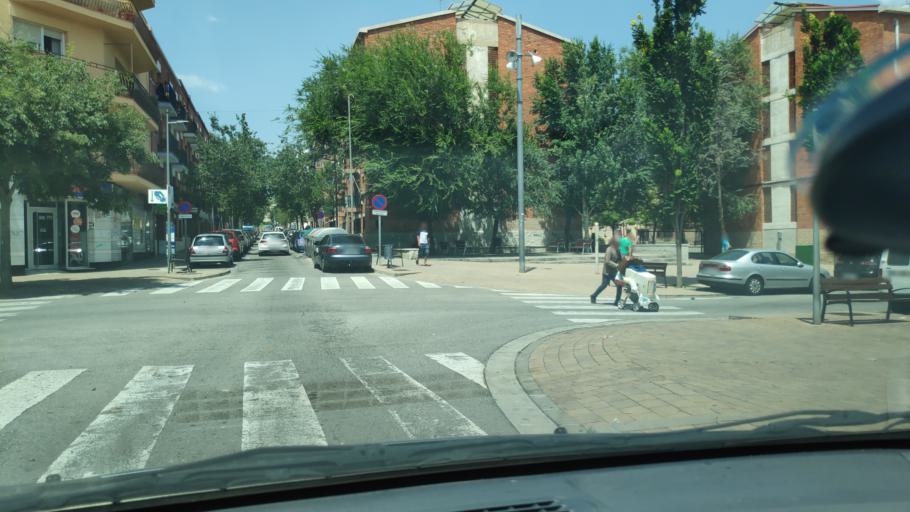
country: ES
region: Catalonia
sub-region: Provincia de Barcelona
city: Terrassa
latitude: 41.5653
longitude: 2.0303
